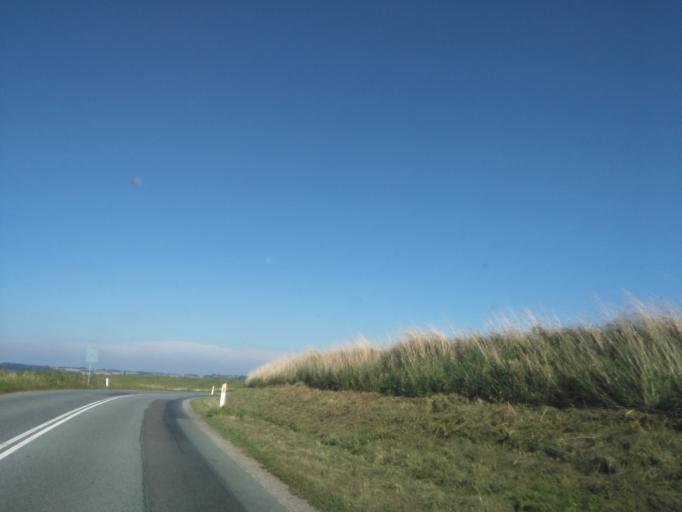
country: DK
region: Central Jutland
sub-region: Syddjurs Kommune
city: Ronde
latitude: 56.2496
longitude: 10.4971
